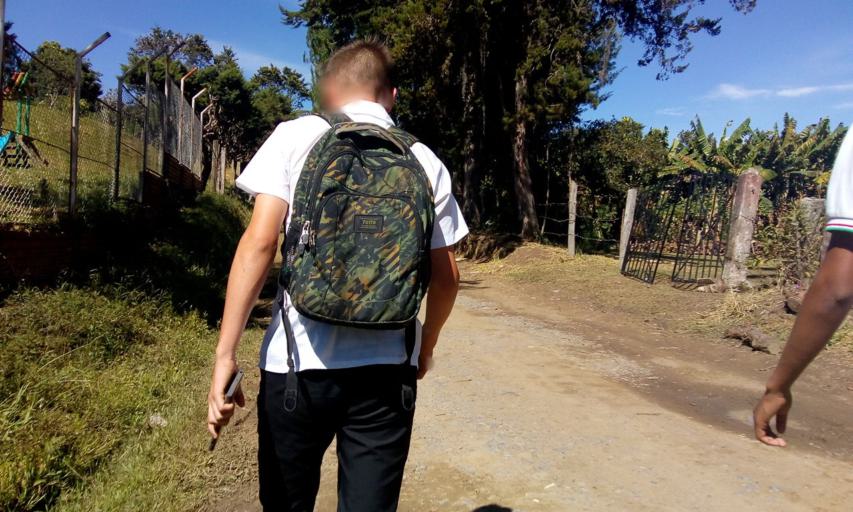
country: CO
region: Santander
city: Guepsa
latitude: 6.0007
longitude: -73.5570
